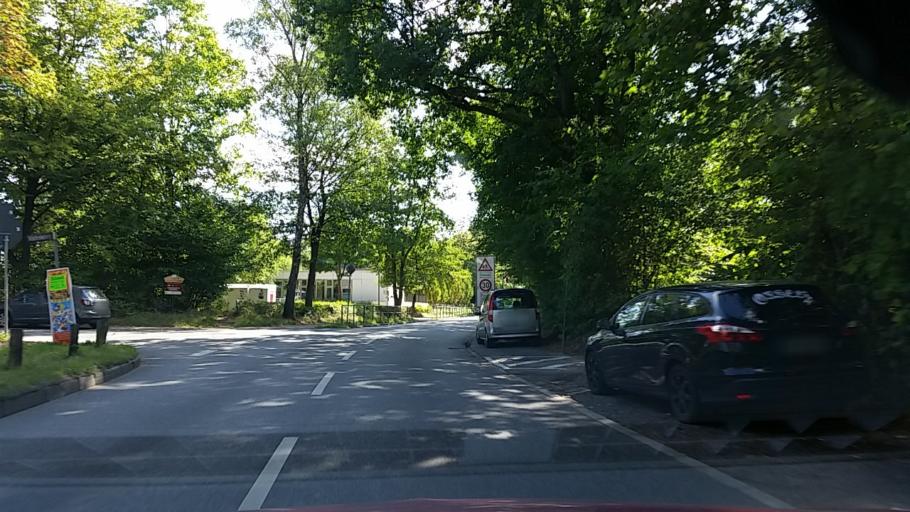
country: DE
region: Hamburg
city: Bergstedt
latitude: 53.6662
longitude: 10.1476
